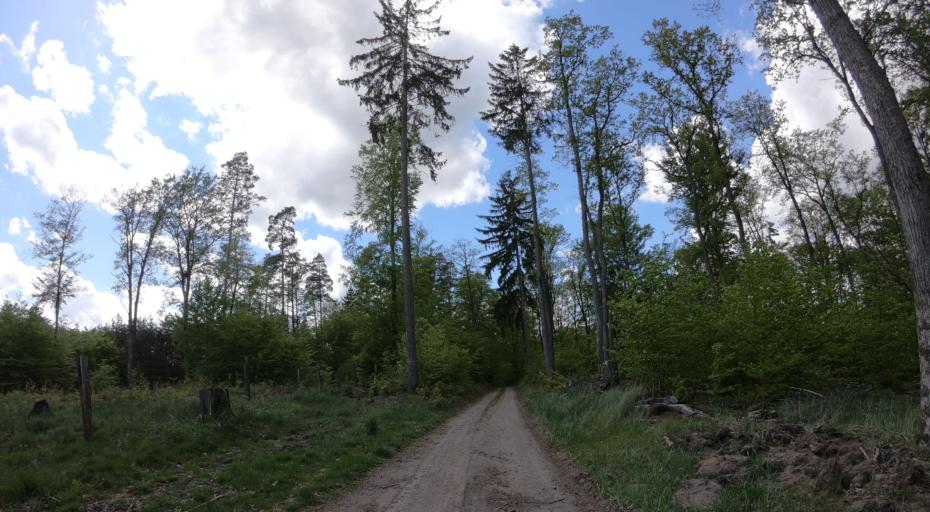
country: PL
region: West Pomeranian Voivodeship
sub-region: Powiat lobeski
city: Lobez
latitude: 53.5973
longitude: 15.6184
